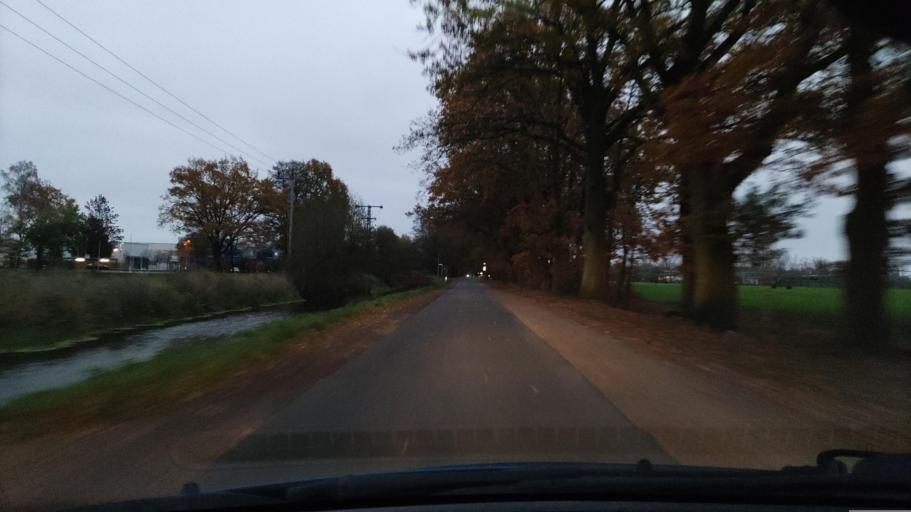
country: DE
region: Mecklenburg-Vorpommern
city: Neu Kaliss
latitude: 53.1814
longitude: 11.2722
